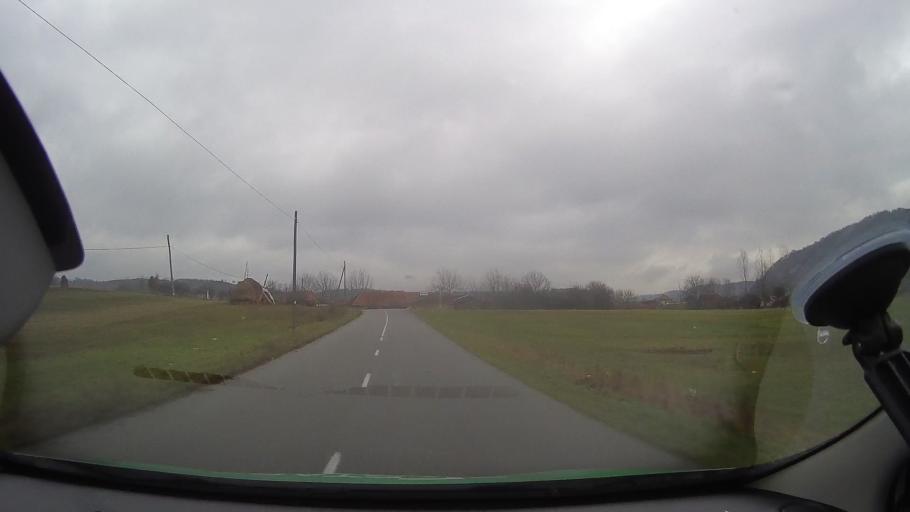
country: RO
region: Hunedoara
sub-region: Comuna Tomesti
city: Tomesti
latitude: 46.1931
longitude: 22.6349
